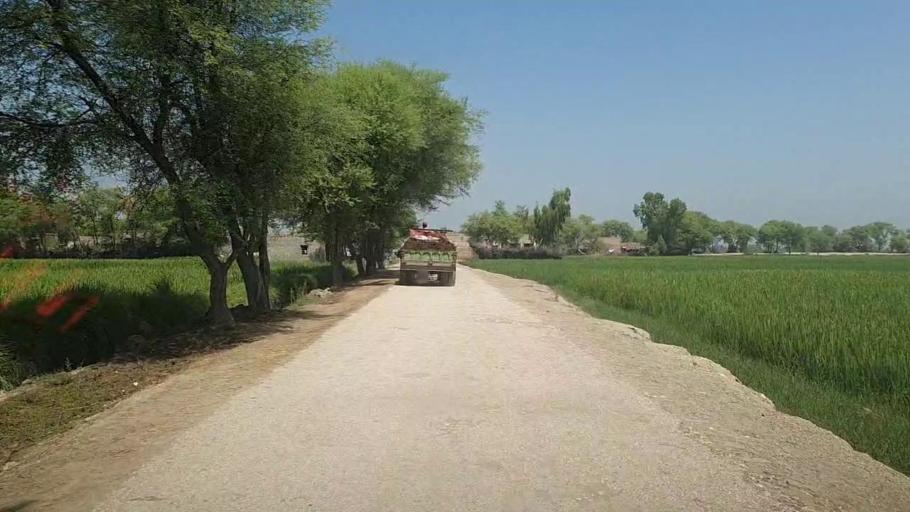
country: PK
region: Sindh
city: Kandhkot
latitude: 28.2949
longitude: 69.2926
